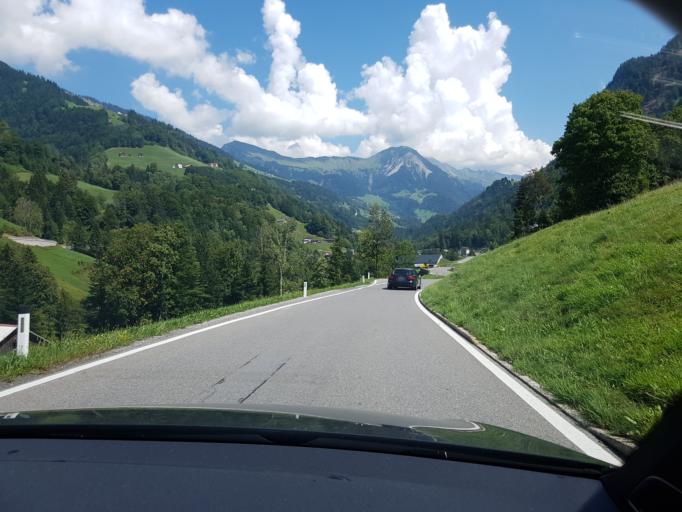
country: AT
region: Vorarlberg
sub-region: Politischer Bezirk Bludenz
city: Raggal
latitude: 47.2225
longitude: 9.8669
